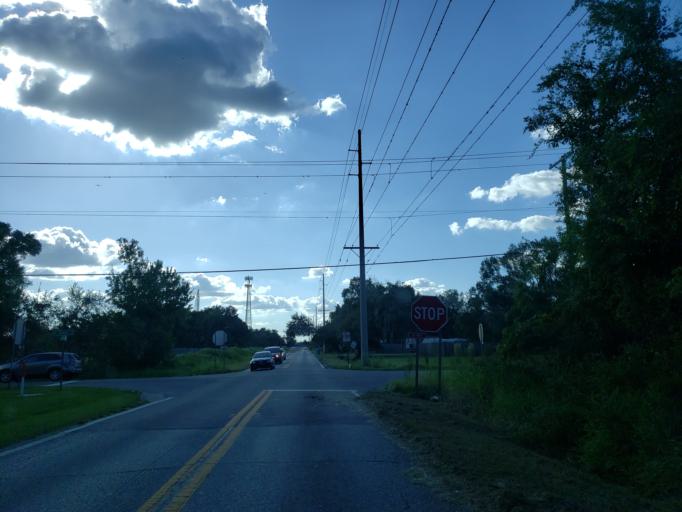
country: US
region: Florida
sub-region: Hillsborough County
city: Dover
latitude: 27.9670
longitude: -82.2194
